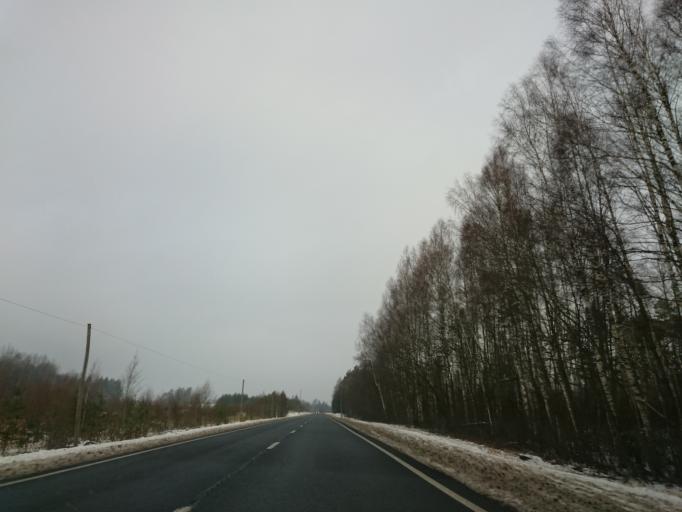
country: LV
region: Pargaujas
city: Stalbe
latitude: 57.3195
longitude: 24.9227
